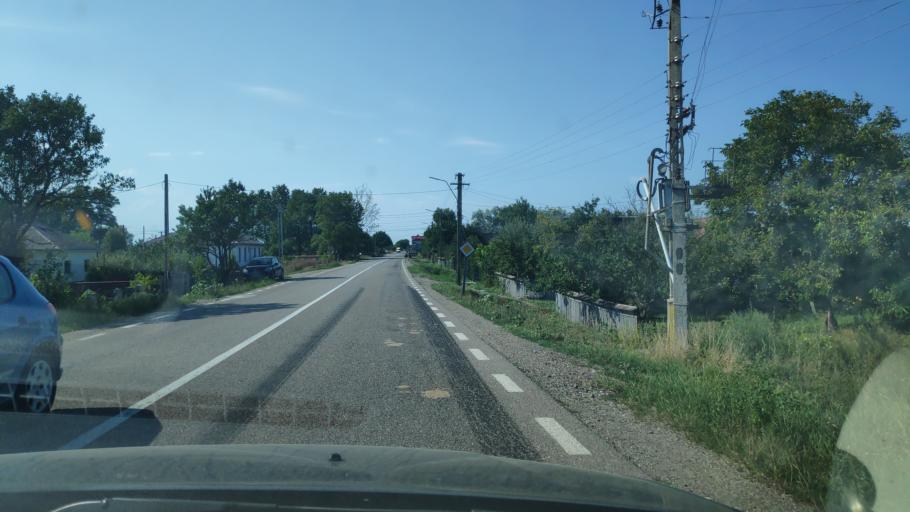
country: RO
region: Suceava
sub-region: Comuna Boroaia
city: Boroaia
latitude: 47.3794
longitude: 26.3187
